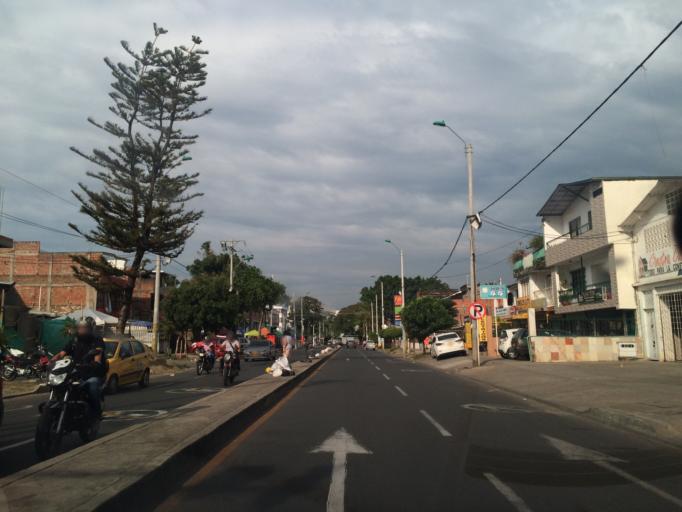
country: CO
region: Valle del Cauca
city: Cali
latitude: 3.3939
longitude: -76.5494
